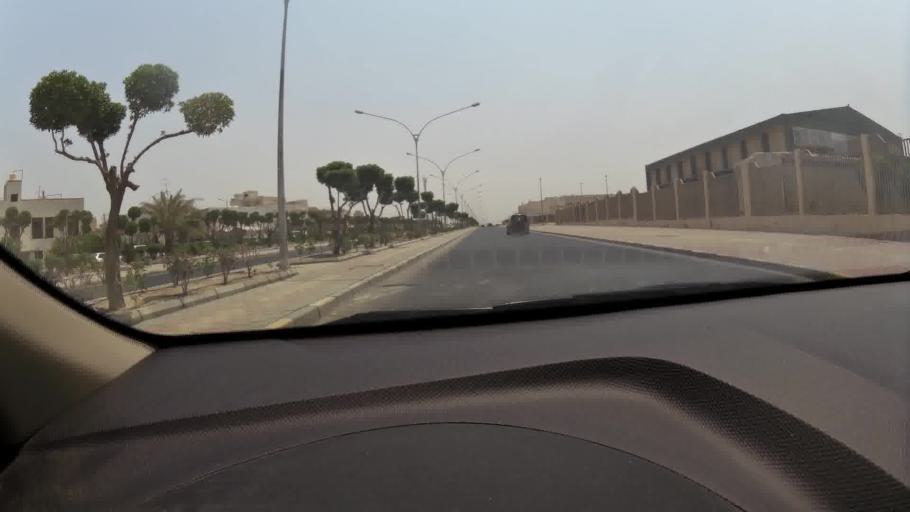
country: KW
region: Al Asimah
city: Ar Rabiyah
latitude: 29.3155
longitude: 47.8189
